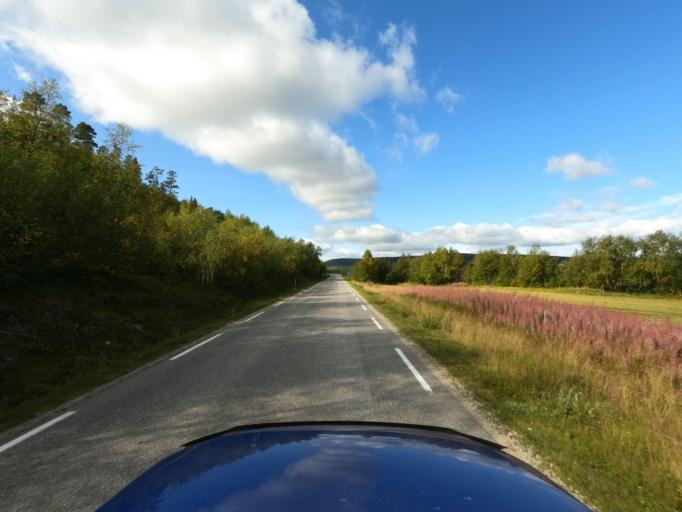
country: NO
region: Finnmark Fylke
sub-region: Karasjok
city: Karasjohka
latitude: 69.4592
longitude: 25.5414
